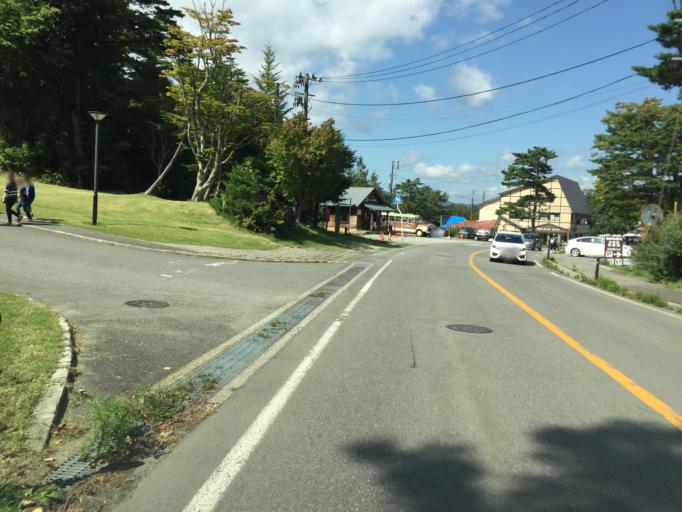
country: JP
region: Fukushima
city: Inawashiro
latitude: 37.6508
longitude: 140.0645
